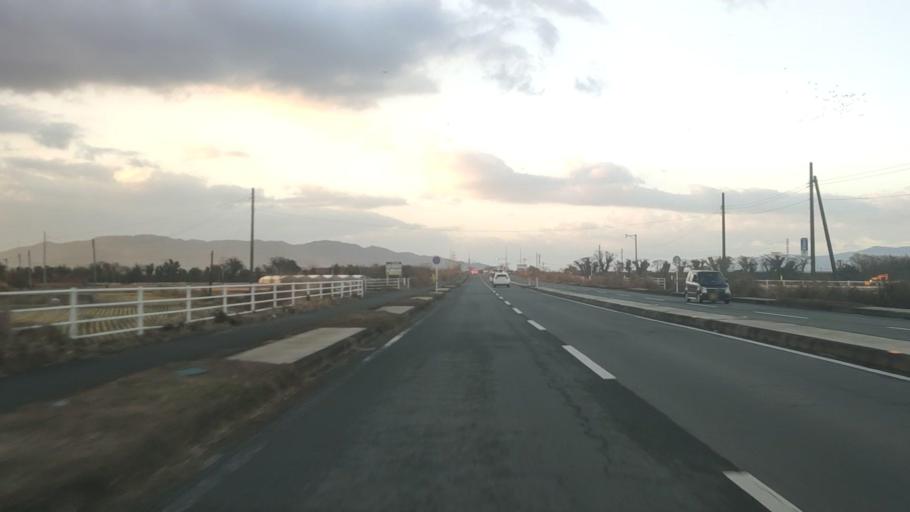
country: JP
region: Kumamoto
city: Kumamoto
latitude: 32.7459
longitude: 130.7064
